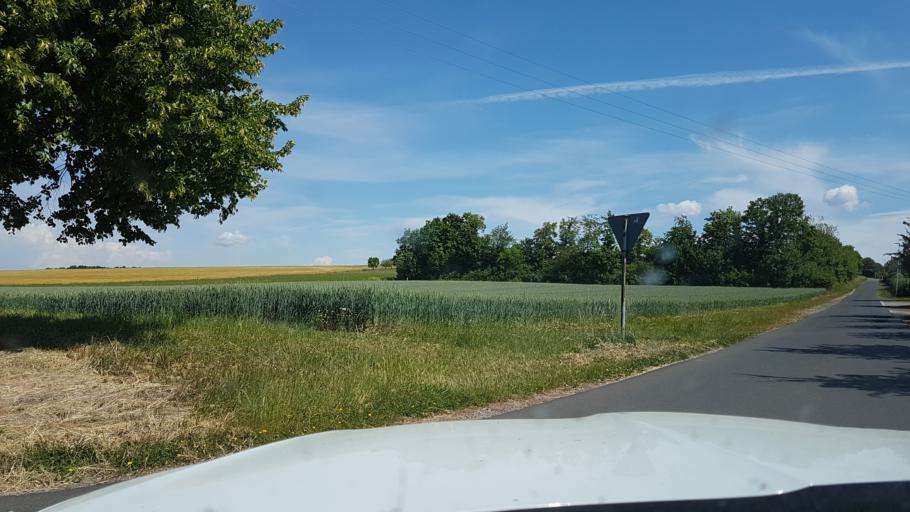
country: DE
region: Bavaria
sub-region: Regierungsbezirk Unterfranken
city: Wonfurt
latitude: 49.9991
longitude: 10.4982
